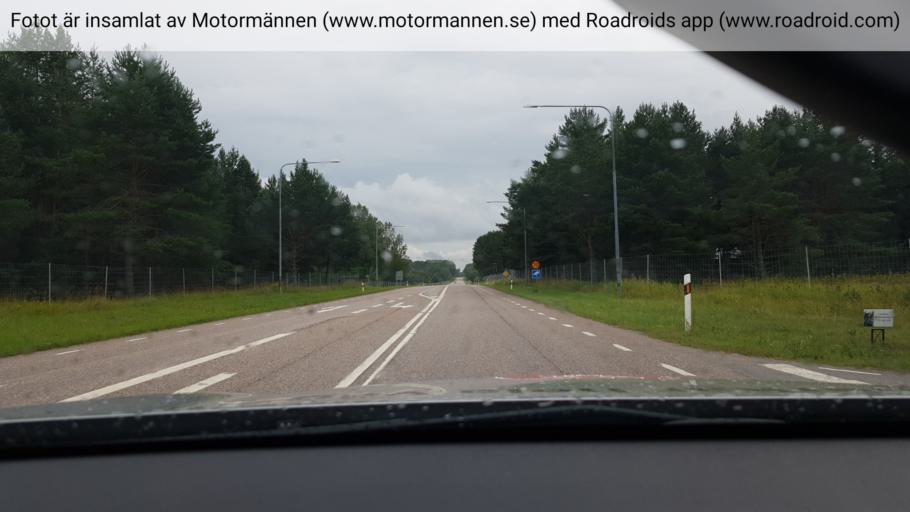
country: SE
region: Uppsala
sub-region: Alvkarleby Kommun
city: AElvkarleby
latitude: 60.5854
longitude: 17.4655
